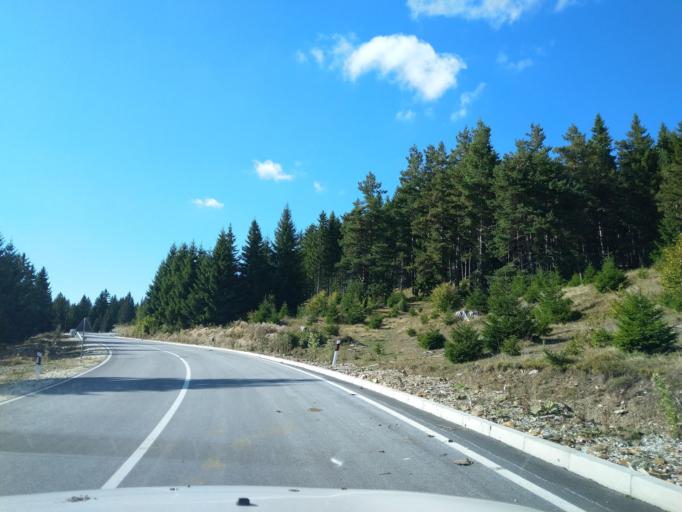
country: RS
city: Sokolovica
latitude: 43.3096
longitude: 20.3004
